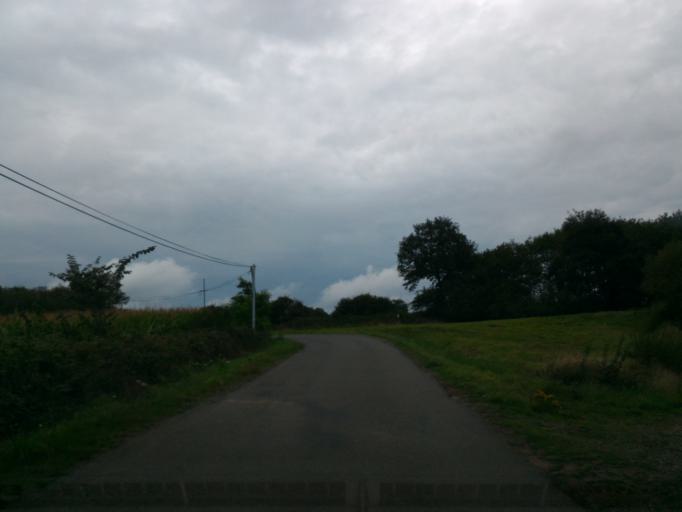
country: FR
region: Poitou-Charentes
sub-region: Departement de la Charente
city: Etagnac
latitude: 45.9063
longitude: 0.7546
